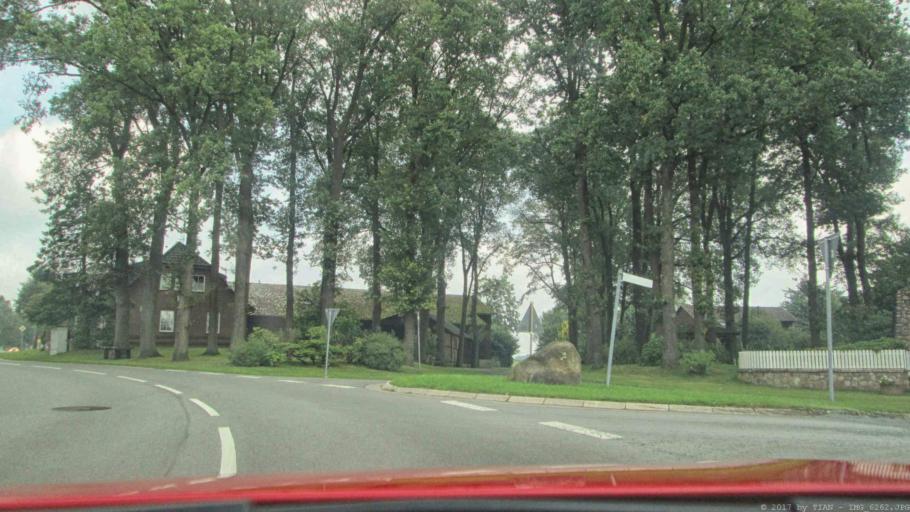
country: DE
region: Lower Saxony
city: Hankensbuttel
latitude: 52.6859
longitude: 10.5758
